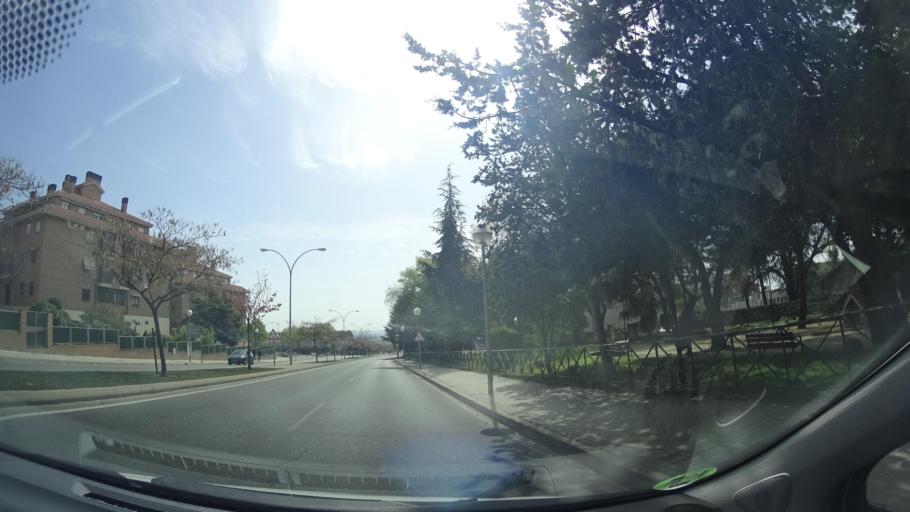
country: ES
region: Madrid
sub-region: Provincia de Madrid
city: Colmenar Viejo
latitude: 40.6540
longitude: -3.7742
